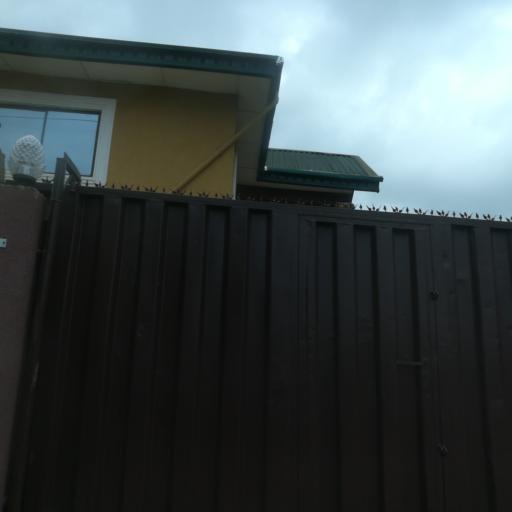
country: NG
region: Lagos
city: Agege
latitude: 6.6046
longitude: 3.2977
